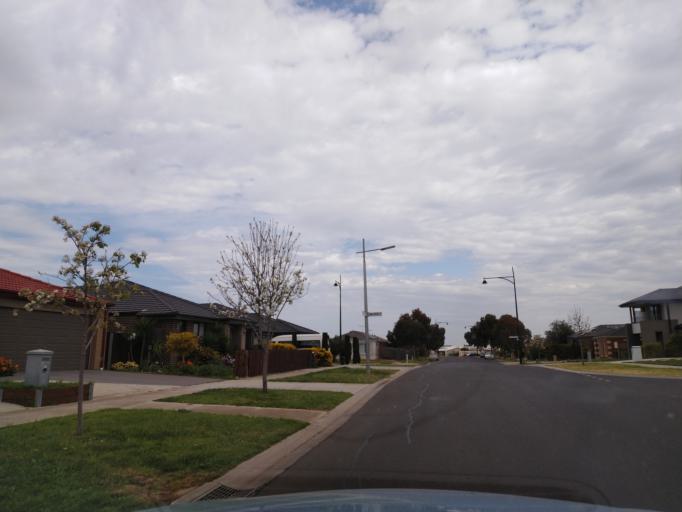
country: AU
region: Victoria
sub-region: Wyndham
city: Williams Landing
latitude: -37.8410
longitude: 144.7111
